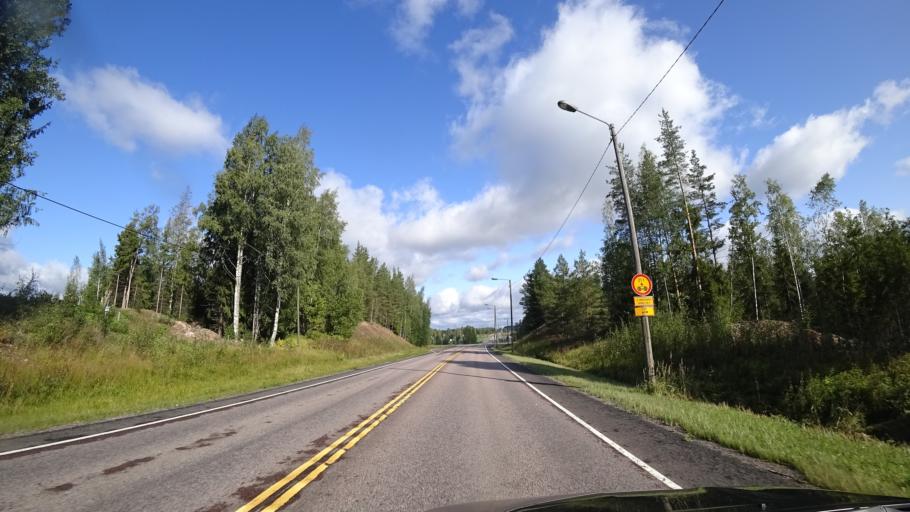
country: FI
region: Uusimaa
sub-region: Helsinki
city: Nurmijaervi
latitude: 60.5093
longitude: 24.9284
